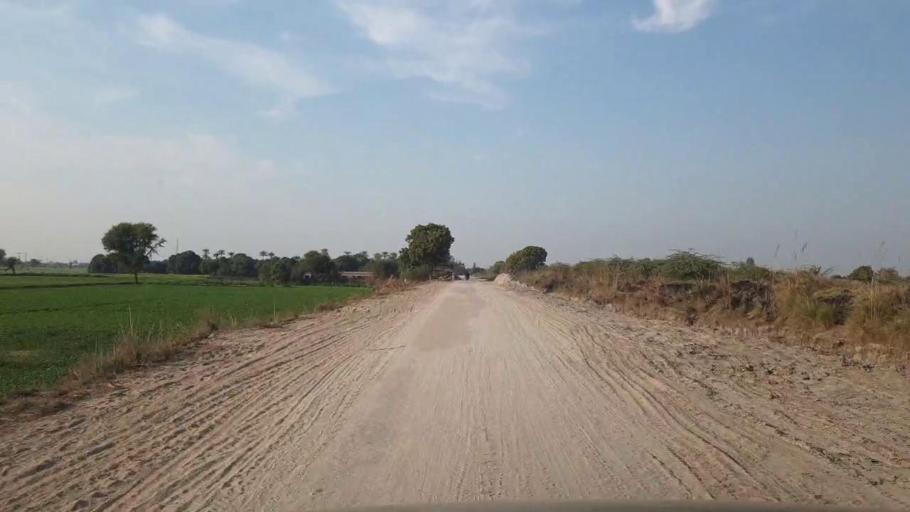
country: PK
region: Sindh
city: Shahpur Chakar
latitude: 26.1514
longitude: 68.6422
